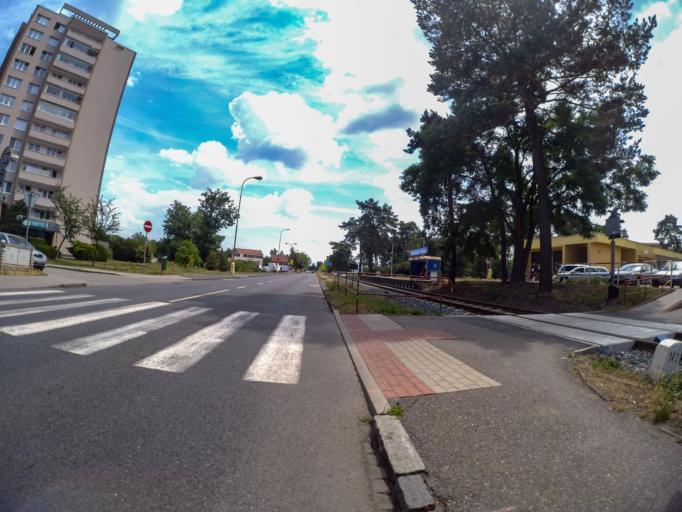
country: CZ
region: Central Bohemia
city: Neratovice
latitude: 50.2571
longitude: 14.5197
